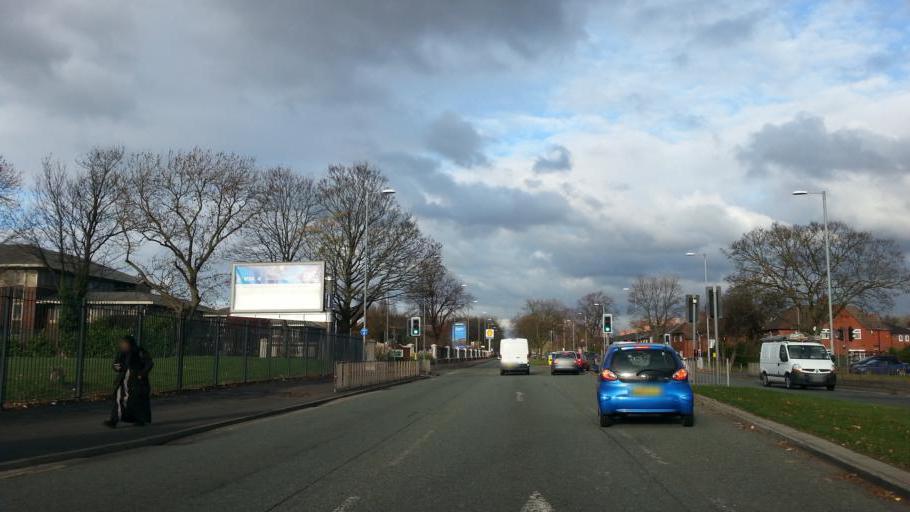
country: GB
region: England
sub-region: Manchester
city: Hulme
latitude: 53.4457
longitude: -2.2445
